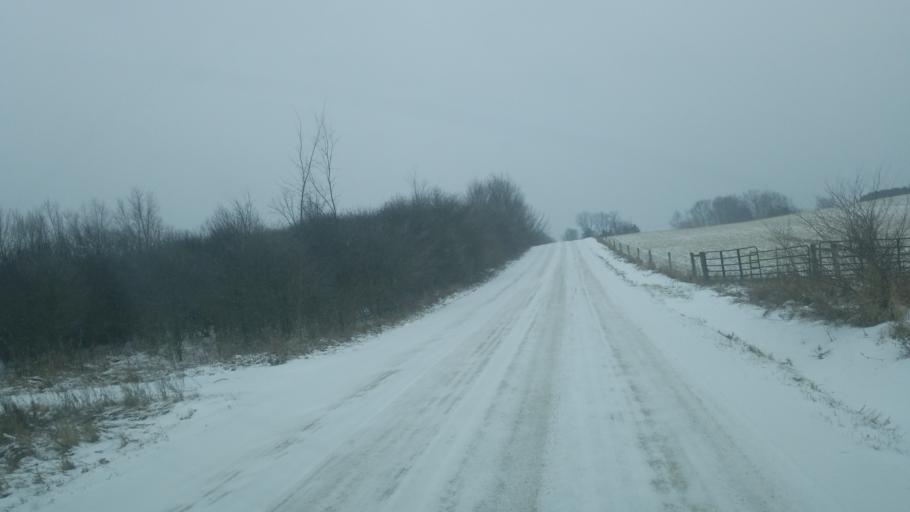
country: US
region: Michigan
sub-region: Osceola County
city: Reed City
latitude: 43.8280
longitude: -85.3939
